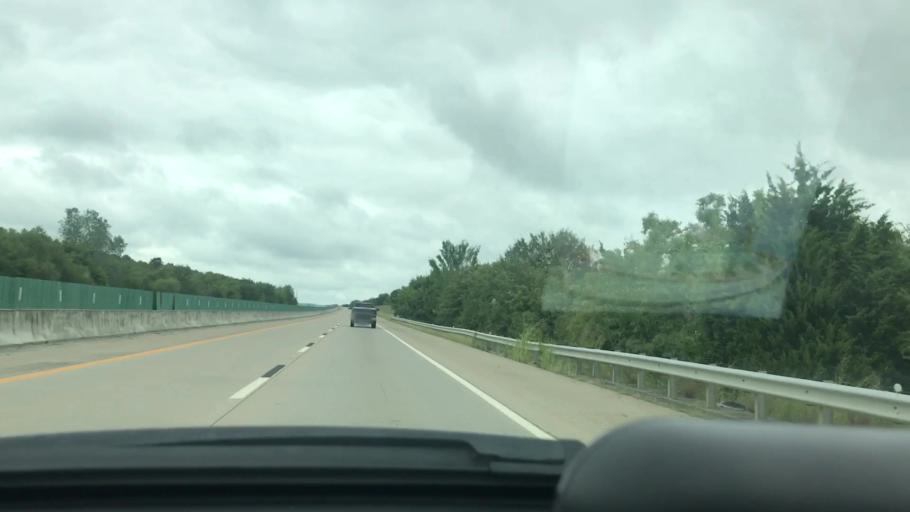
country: US
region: Oklahoma
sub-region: Pittsburg County
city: Krebs
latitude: 35.0294
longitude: -95.7143
